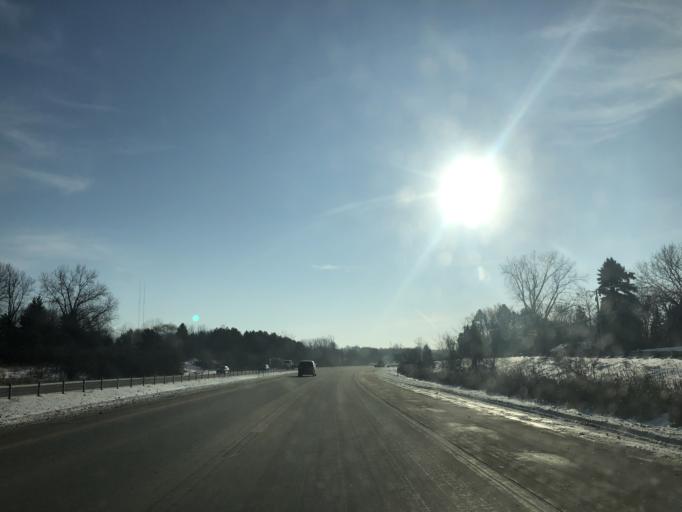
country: US
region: Minnesota
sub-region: Ramsey County
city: Shoreview
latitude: 45.0758
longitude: -93.1723
